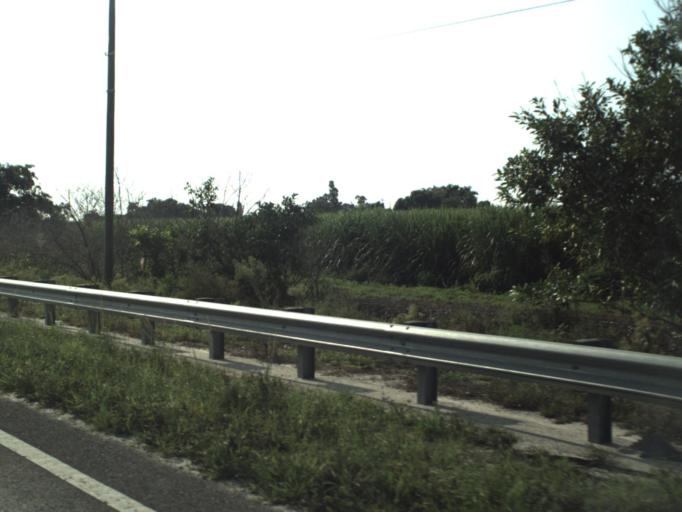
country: US
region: Florida
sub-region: Palm Beach County
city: South Bay
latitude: 26.6959
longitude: -80.8111
